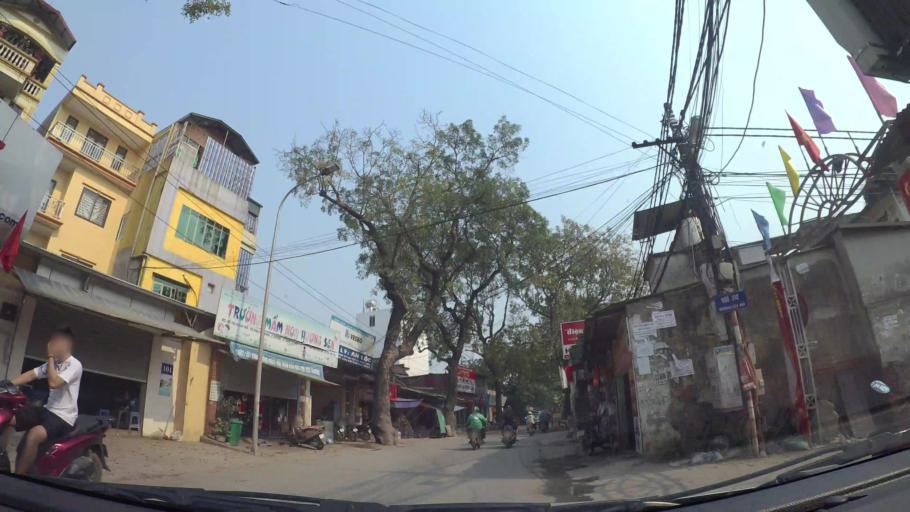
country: VN
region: Ha Noi
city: Ha Dong
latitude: 20.9997
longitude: 105.7514
